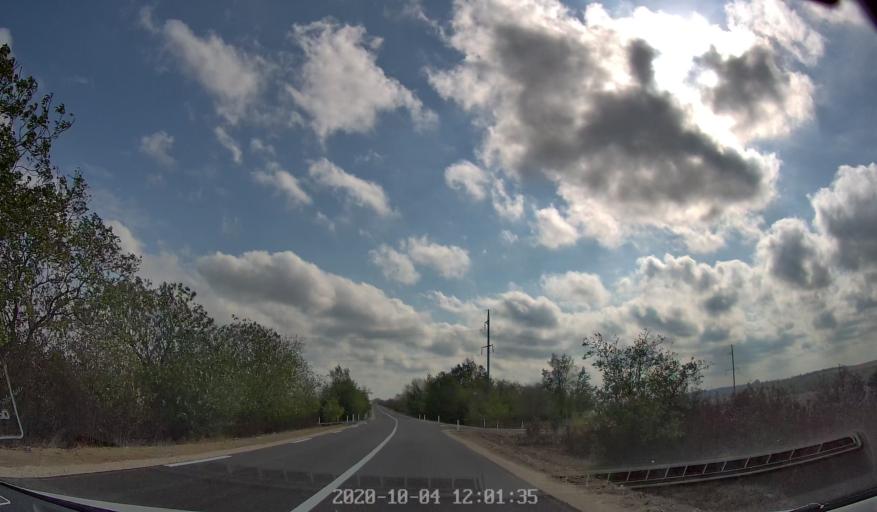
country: MD
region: Rezina
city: Saharna
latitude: 47.6236
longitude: 28.8915
